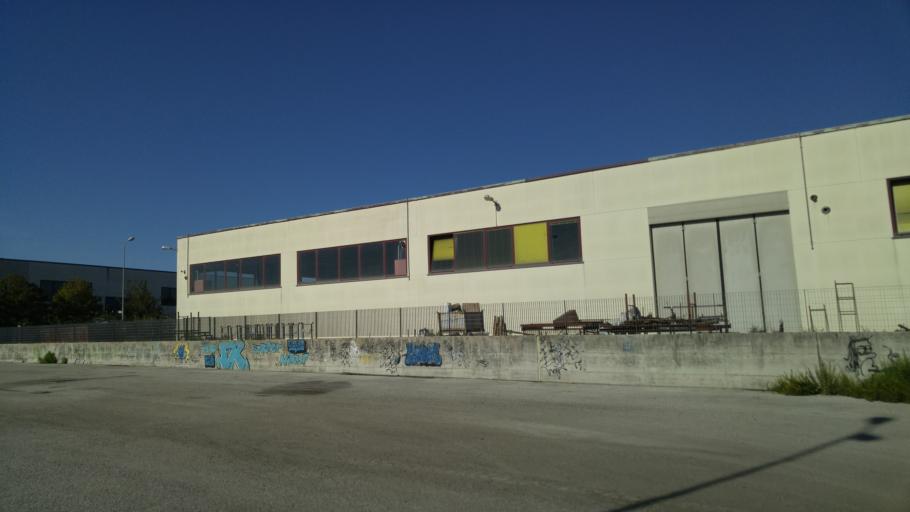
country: IT
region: The Marches
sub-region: Provincia di Pesaro e Urbino
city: Lucrezia
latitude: 43.7676
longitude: 12.9623
